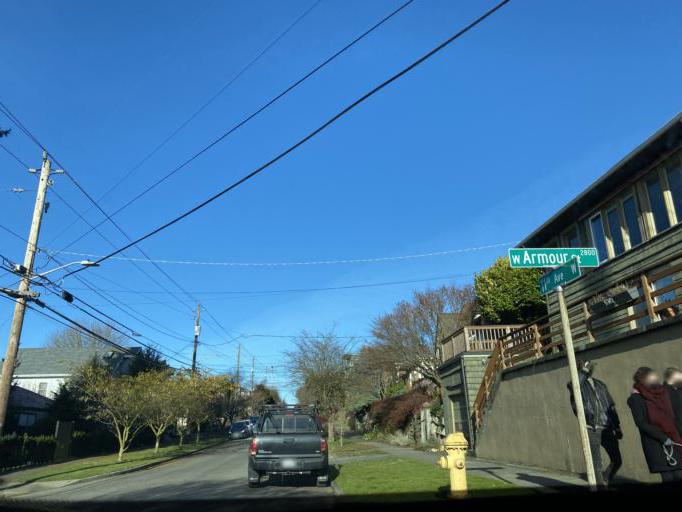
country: US
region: Washington
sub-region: King County
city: Seattle
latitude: 47.6450
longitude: -122.3715
